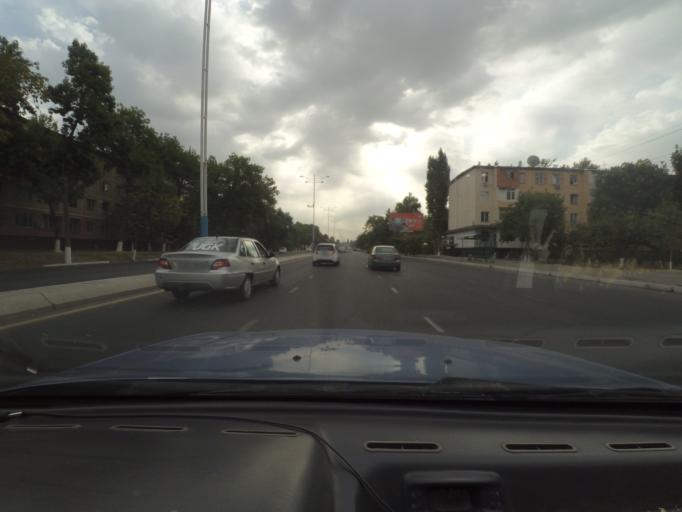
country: UZ
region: Toshkent
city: Salor
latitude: 41.3548
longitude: 69.3630
